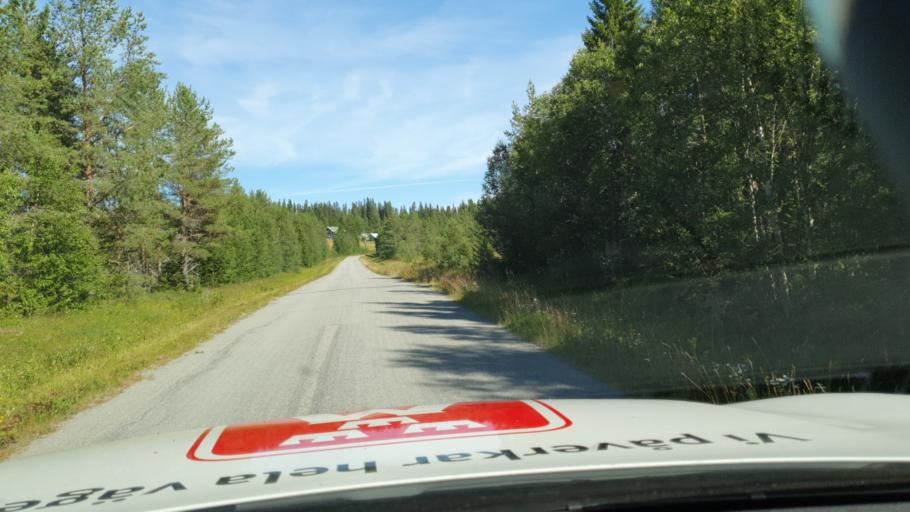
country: SE
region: Jaemtland
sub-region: Krokoms Kommun
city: Krokom
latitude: 63.7577
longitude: 14.4197
